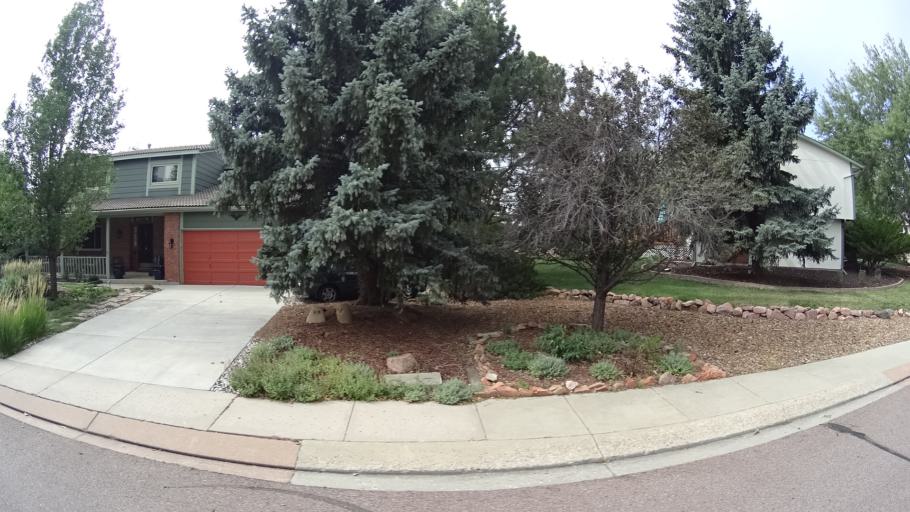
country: US
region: Colorado
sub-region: El Paso County
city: Air Force Academy
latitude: 38.9261
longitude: -104.8359
